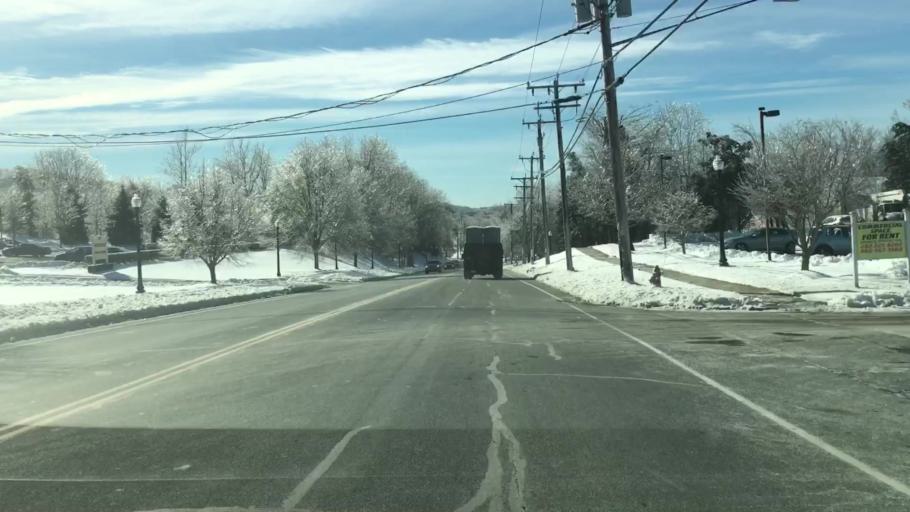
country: US
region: Connecticut
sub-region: New Haven County
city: Southbury
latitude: 41.4754
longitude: -73.2191
